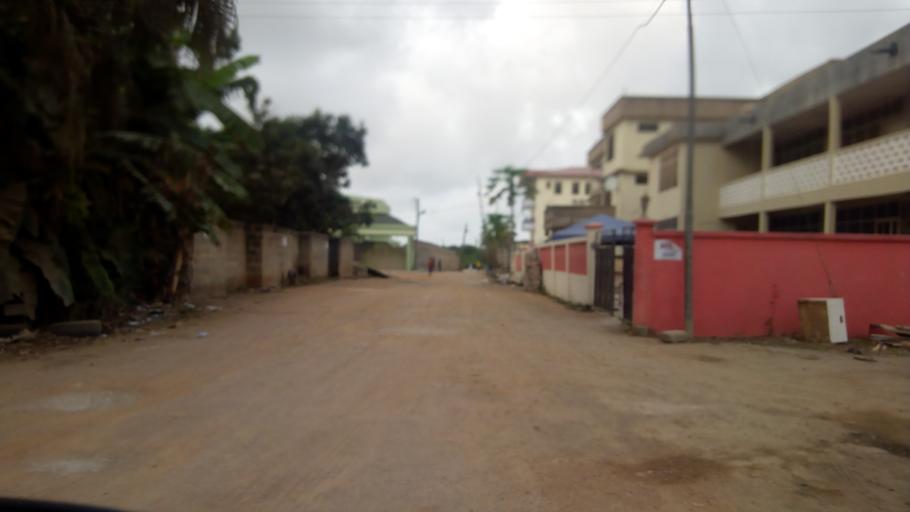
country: GH
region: Central
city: Cape Coast
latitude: 5.1259
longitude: -1.2777
